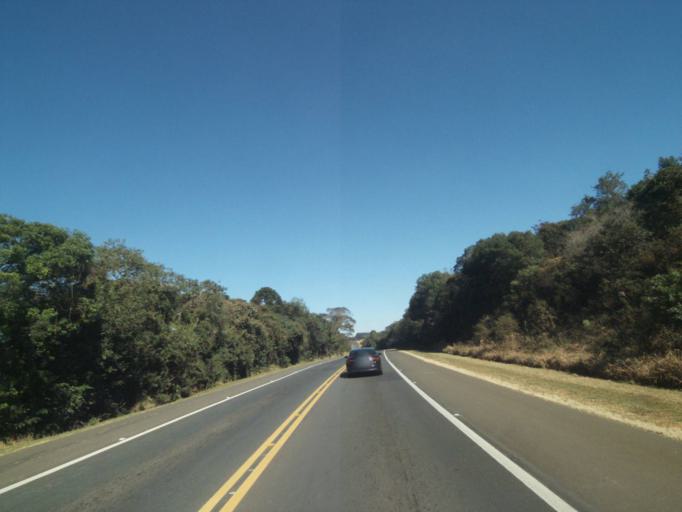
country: BR
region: Parana
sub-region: Tibagi
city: Tibagi
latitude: -24.7339
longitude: -50.5371
